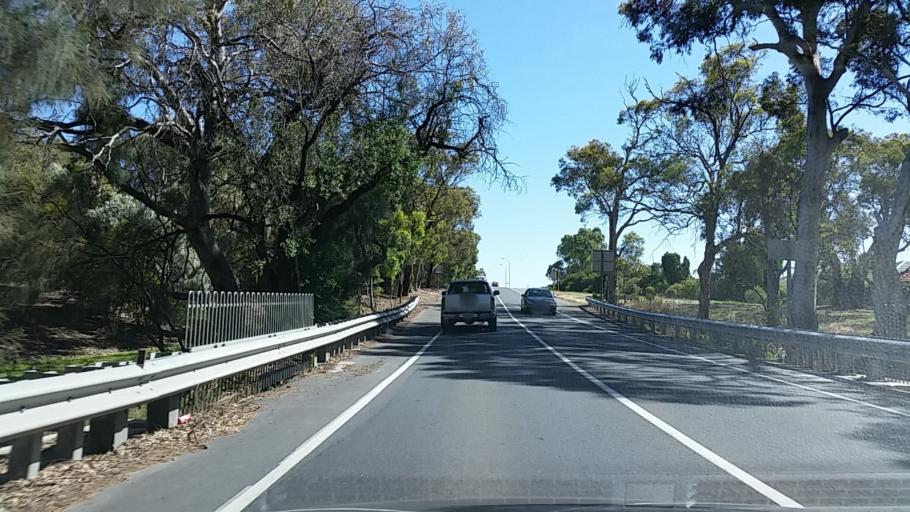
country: AU
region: South Australia
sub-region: Tea Tree Gully
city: Golden Grove
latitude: -34.7966
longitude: 138.7081
